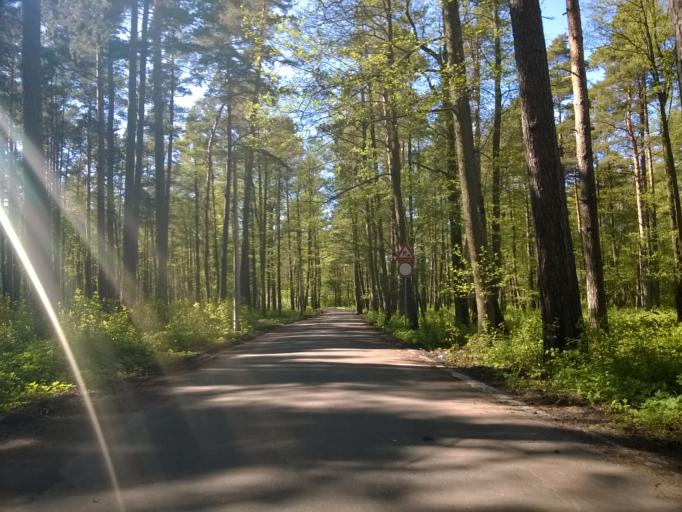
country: LV
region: Jurmala
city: Jurmala
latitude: 56.9580
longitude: 23.6656
